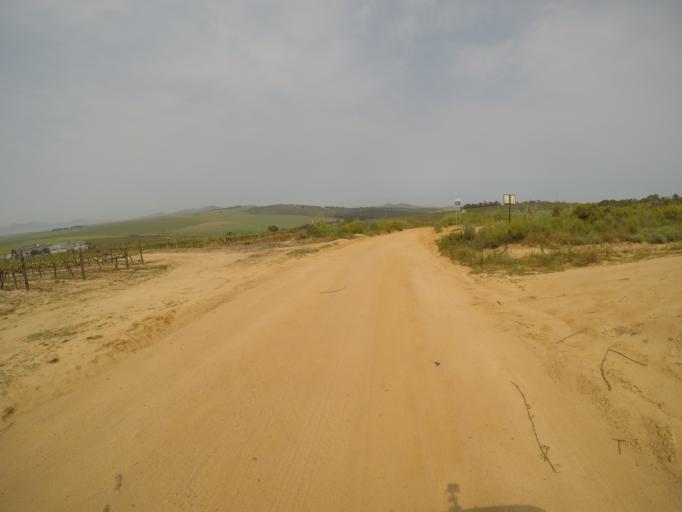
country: ZA
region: Western Cape
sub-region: West Coast District Municipality
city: Malmesbury
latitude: -33.4474
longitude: 18.7472
